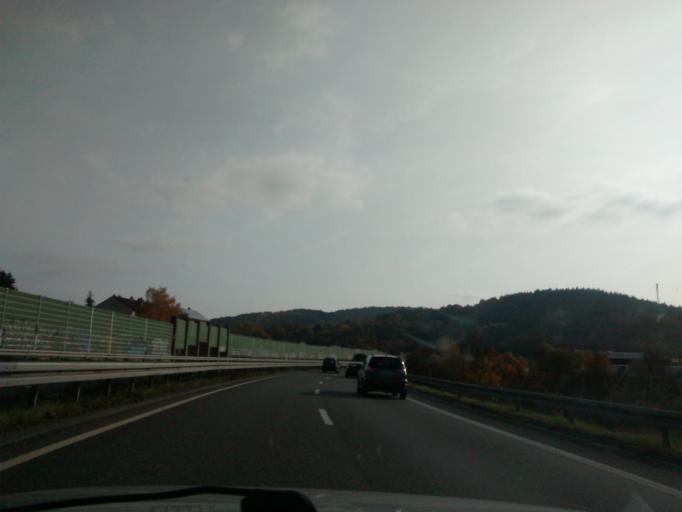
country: DE
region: Hesse
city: Herborn
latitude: 50.7033
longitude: 8.3114
